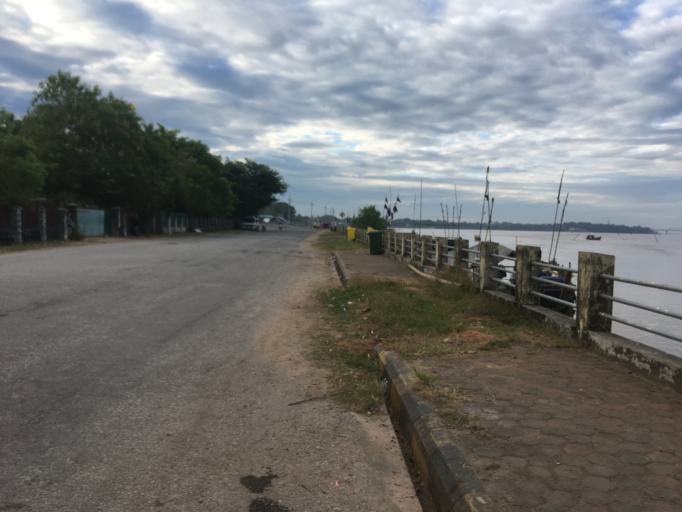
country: MM
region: Mon
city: Mawlamyine
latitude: 16.4654
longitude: 97.6222
